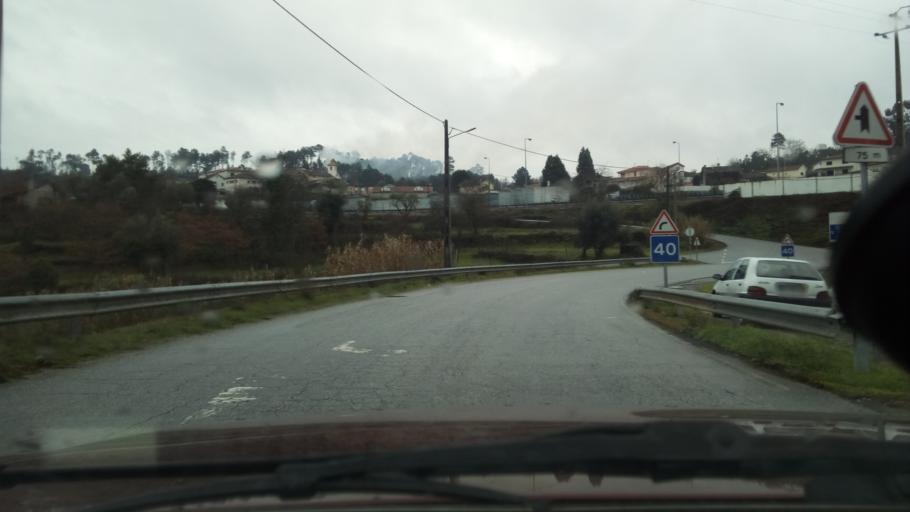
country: PT
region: Viseu
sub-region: Mangualde
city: Mangualde
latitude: 40.6294
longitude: -7.8008
